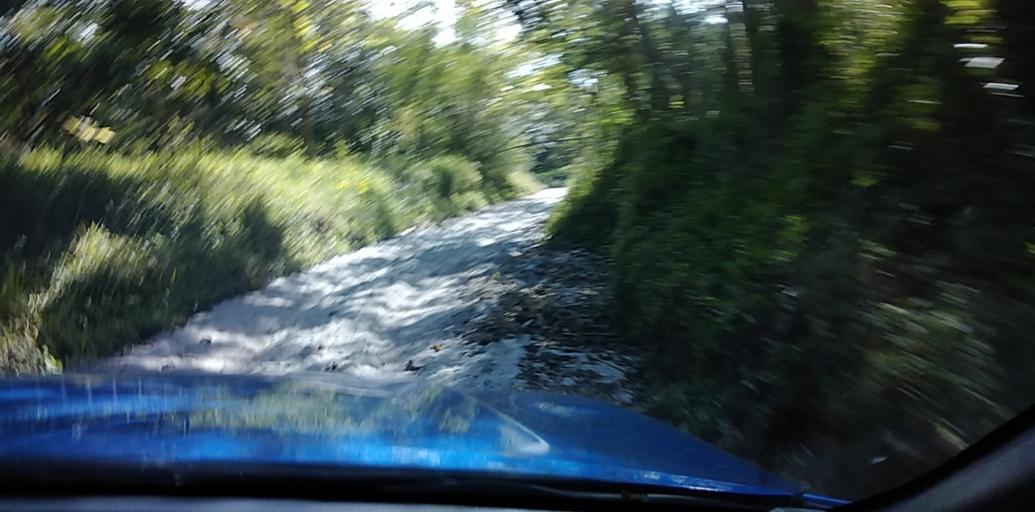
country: PH
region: Central Luzon
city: Santol
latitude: 15.1702
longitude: 120.4805
